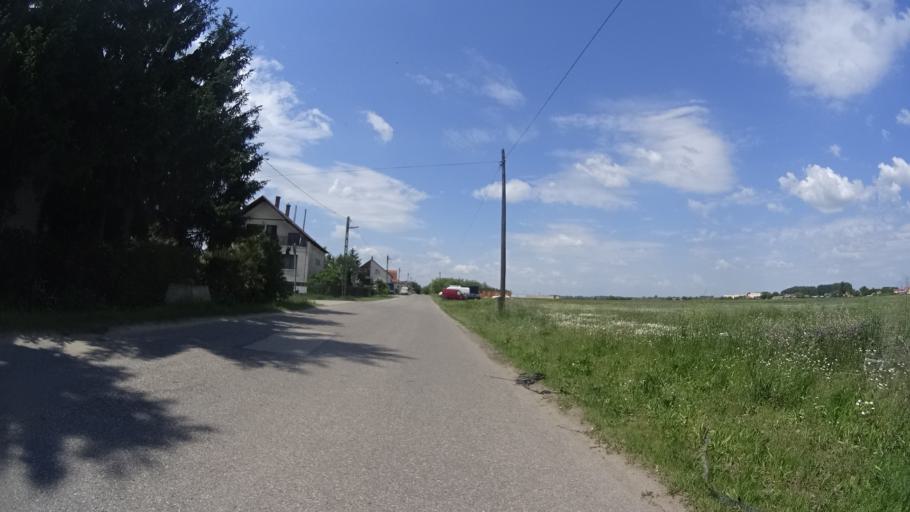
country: HU
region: Bacs-Kiskun
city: Tiszakecske
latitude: 46.9454
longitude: 20.0926
